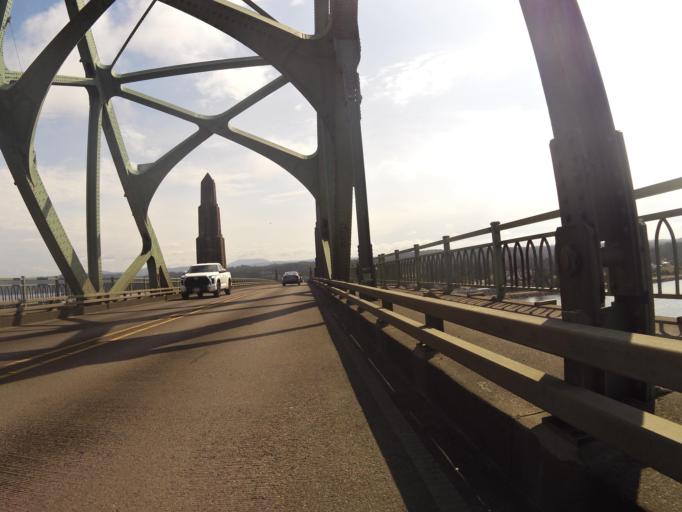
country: US
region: Oregon
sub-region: Lincoln County
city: Newport
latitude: 44.6228
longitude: -124.0577
